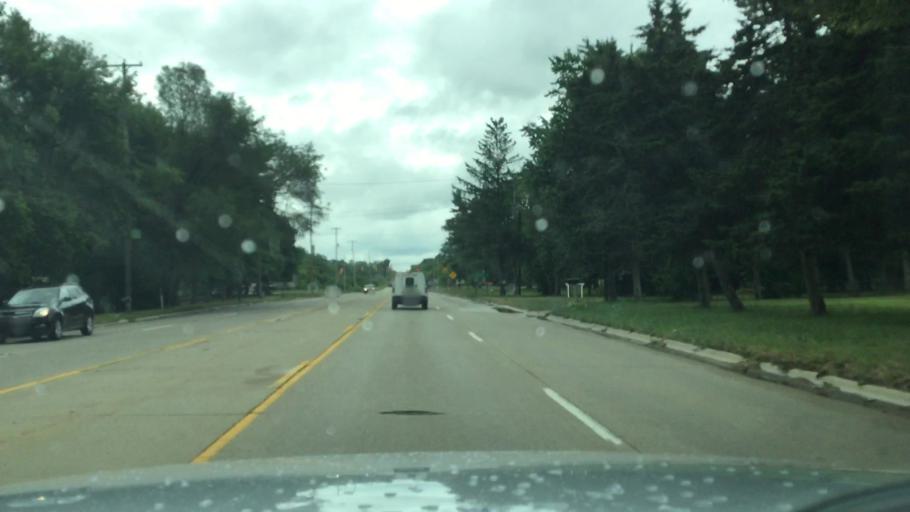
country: US
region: Michigan
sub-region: Genesee County
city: Flushing
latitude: 43.0420
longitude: -83.7738
